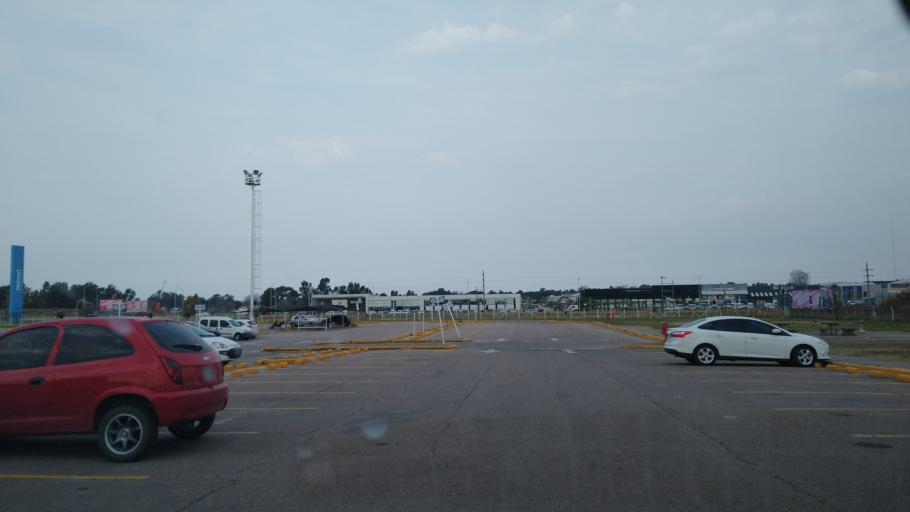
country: AR
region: Buenos Aires
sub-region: Partido de Bahia Blanca
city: Bahia Blanca
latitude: -38.6861
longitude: -62.2320
